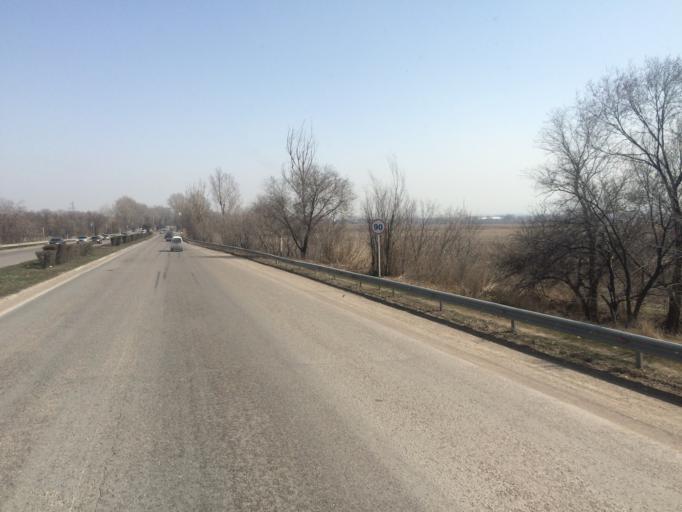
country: KZ
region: Almaty Oblysy
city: Burunday
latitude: 43.2233
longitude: 76.5962
